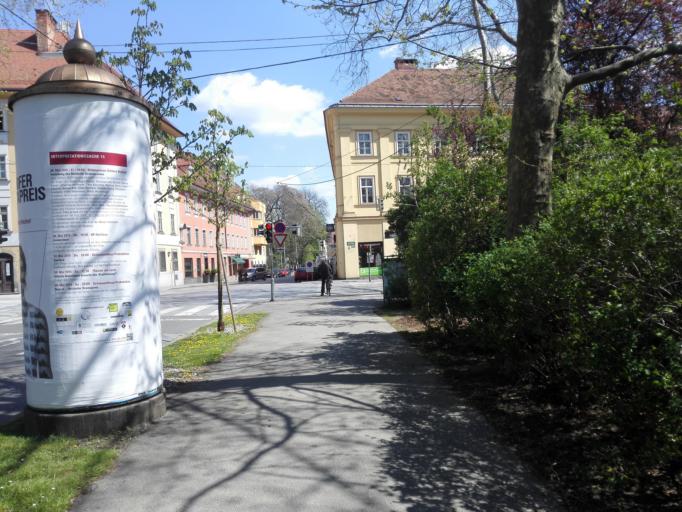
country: AT
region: Styria
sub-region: Graz Stadt
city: Graz
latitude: 47.0721
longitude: 15.4471
